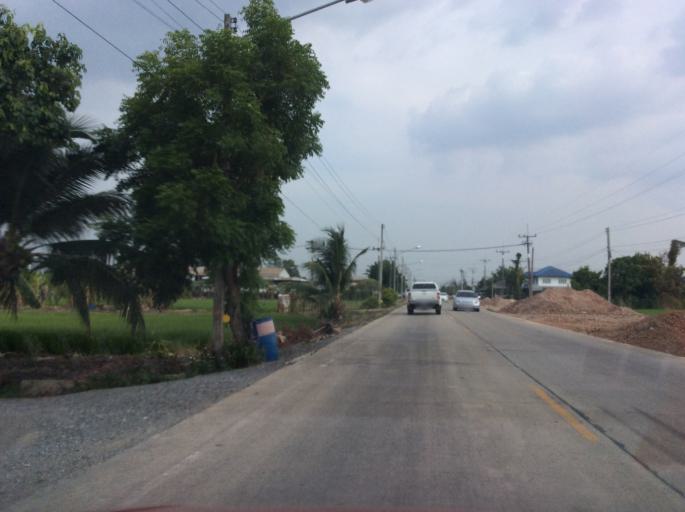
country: TH
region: Pathum Thani
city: Lam Luk Ka
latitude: 13.9692
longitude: 100.7260
